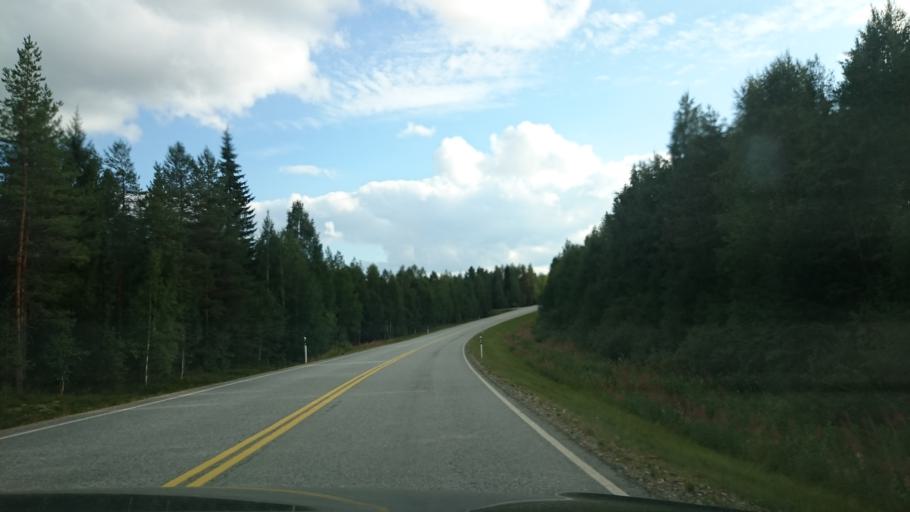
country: FI
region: Kainuu
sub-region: Kehys-Kainuu
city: Kuhmo
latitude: 64.5201
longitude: 29.9464
